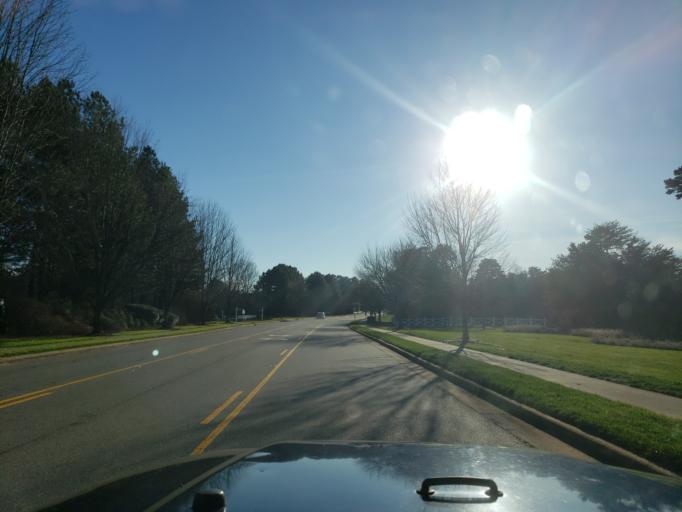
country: US
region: North Carolina
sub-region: Catawba County
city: Lake Norman of Catawba
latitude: 35.5380
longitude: -80.9176
